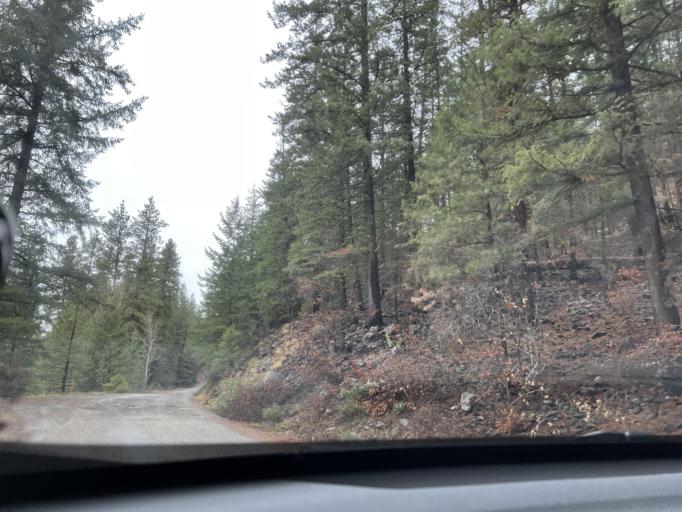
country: US
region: Washington
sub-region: Okanogan County
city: Brewster
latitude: 48.5694
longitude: -120.1715
